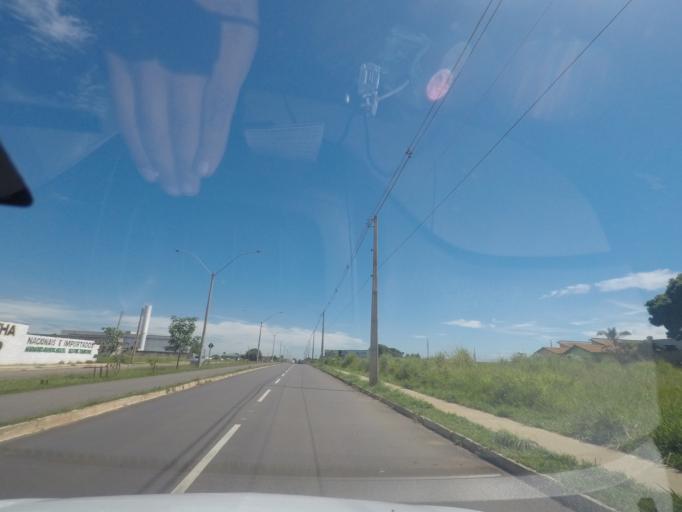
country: BR
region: Goias
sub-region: Aparecida De Goiania
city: Aparecida de Goiania
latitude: -16.7912
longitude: -49.3297
